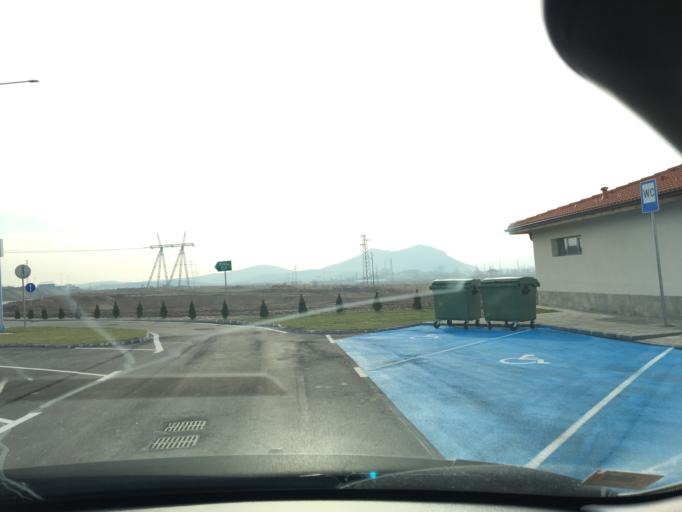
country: BG
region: Blagoevgrad
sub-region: Obshtina Sandanski
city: Sandanski
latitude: 41.5123
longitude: 23.2712
